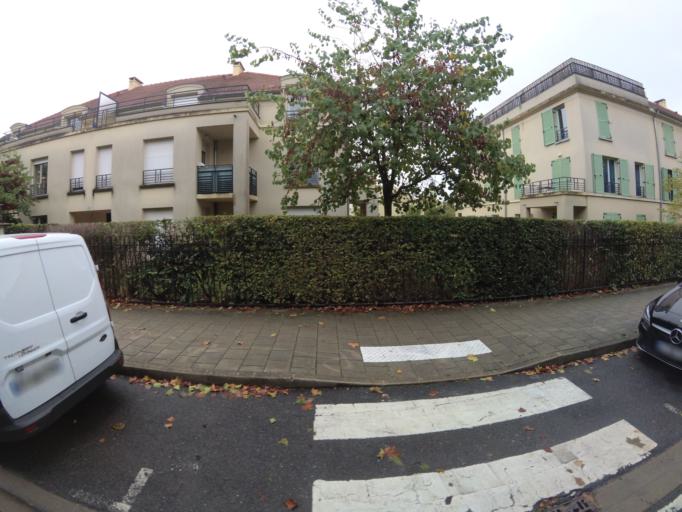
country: FR
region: Ile-de-France
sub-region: Departement de Seine-et-Marne
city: Conches-sur-Gondoire
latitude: 48.8393
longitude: 2.7254
